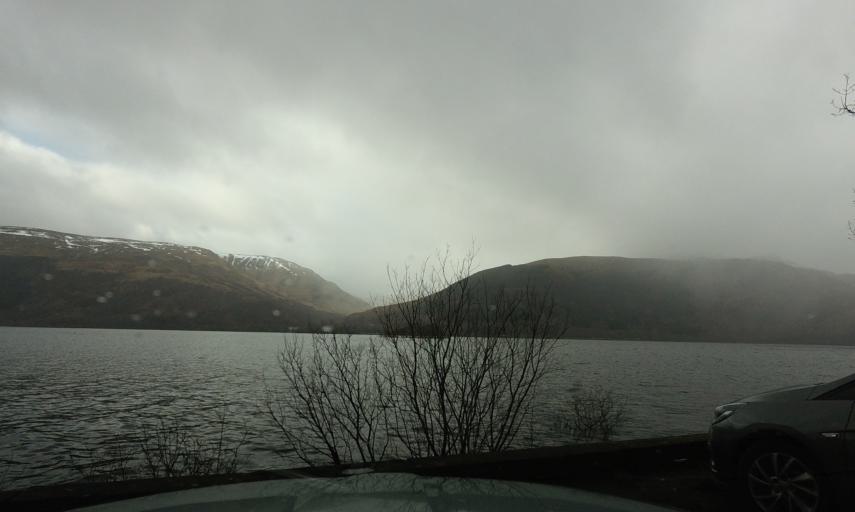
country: GB
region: Scotland
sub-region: West Dunbartonshire
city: Balloch
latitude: 56.1516
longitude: -4.6425
